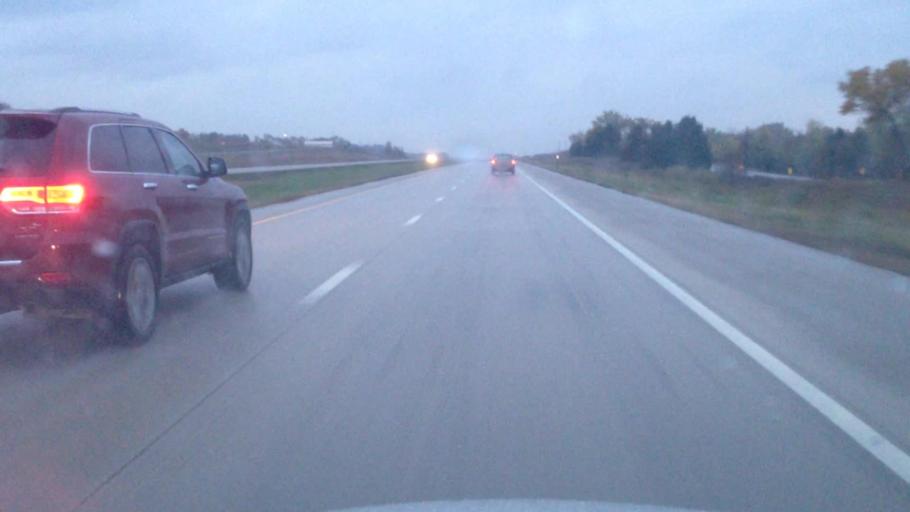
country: US
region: Kansas
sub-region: Douglas County
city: Baldwin City
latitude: 38.8098
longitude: -95.2692
